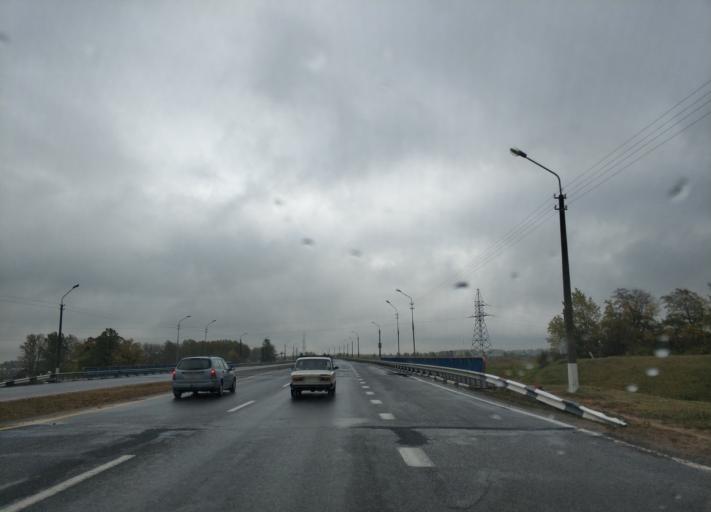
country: BY
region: Vitebsk
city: Vitebsk
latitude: 55.1926
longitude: 30.1269
